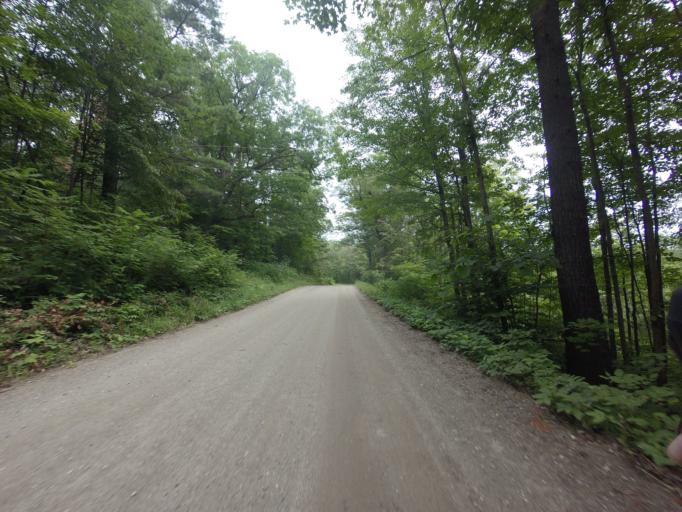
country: CA
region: Ontario
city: Perth
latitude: 44.7210
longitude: -76.6261
